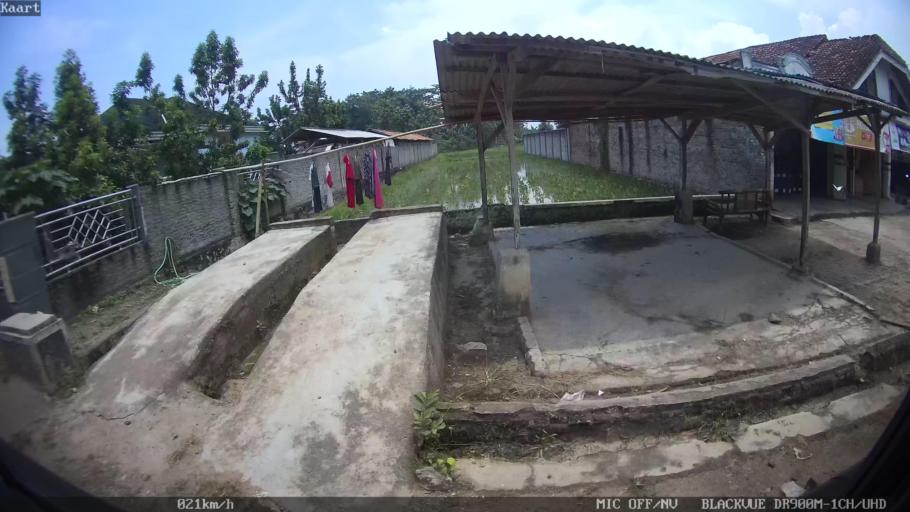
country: ID
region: Lampung
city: Natar
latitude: -5.3121
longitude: 105.2175
